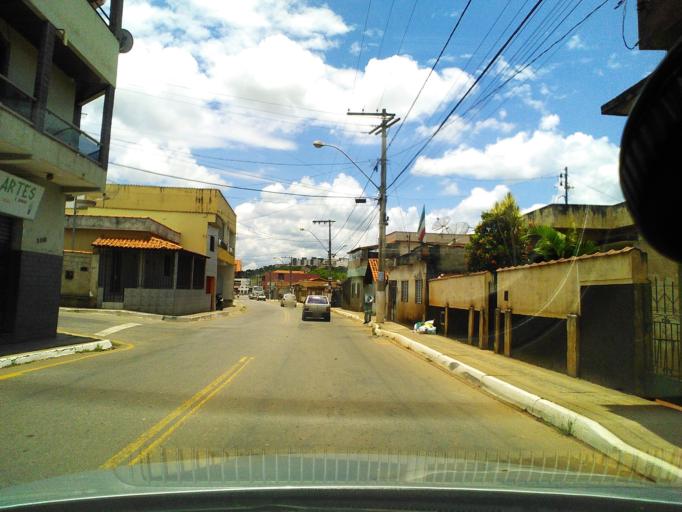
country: BR
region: Minas Gerais
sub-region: Tres Coracoes
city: Tres Coracoes
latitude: -21.7140
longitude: -45.2629
